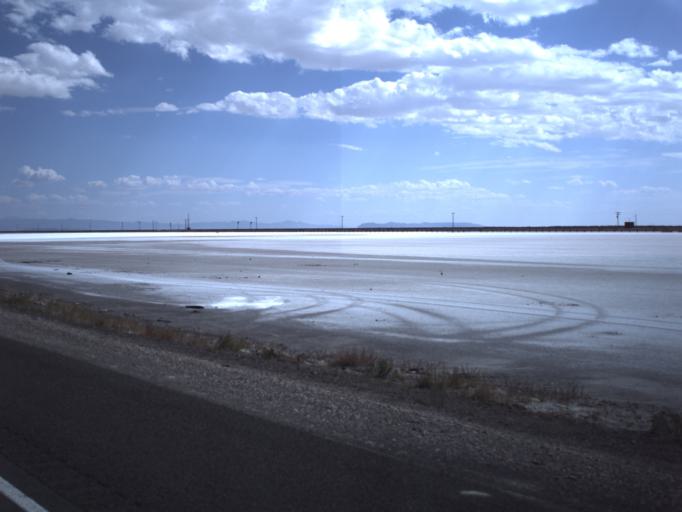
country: US
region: Utah
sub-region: Tooele County
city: Wendover
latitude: 40.7347
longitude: -113.6692
